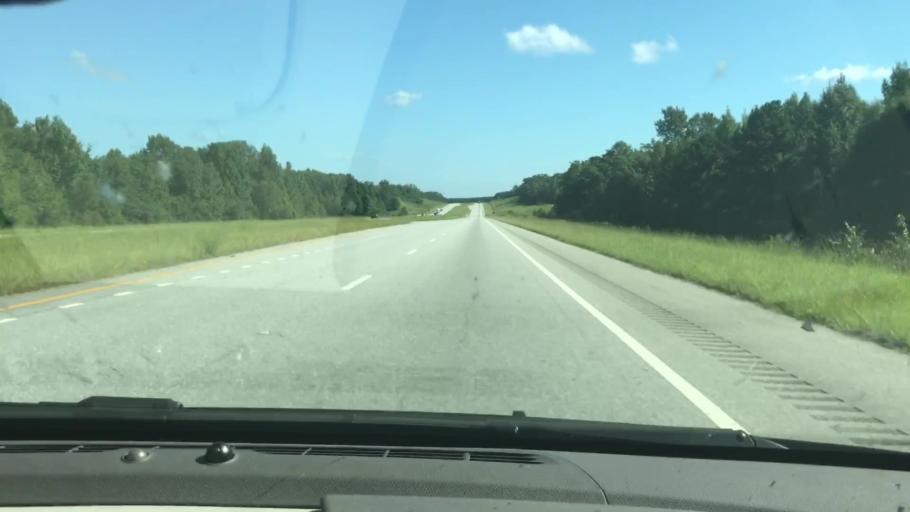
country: US
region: Alabama
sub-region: Russell County
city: Ladonia
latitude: 32.1972
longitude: -85.1784
